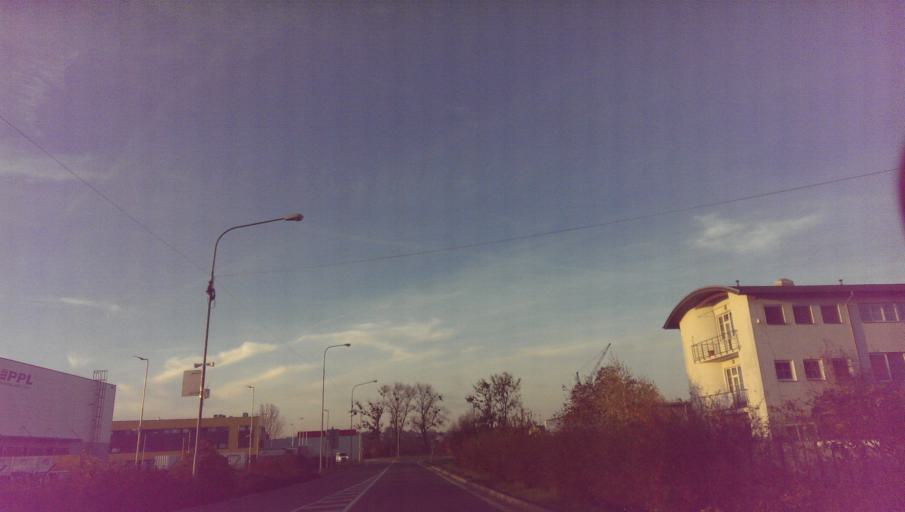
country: CZ
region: Zlin
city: Tecovice
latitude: 49.2101
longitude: 17.5910
